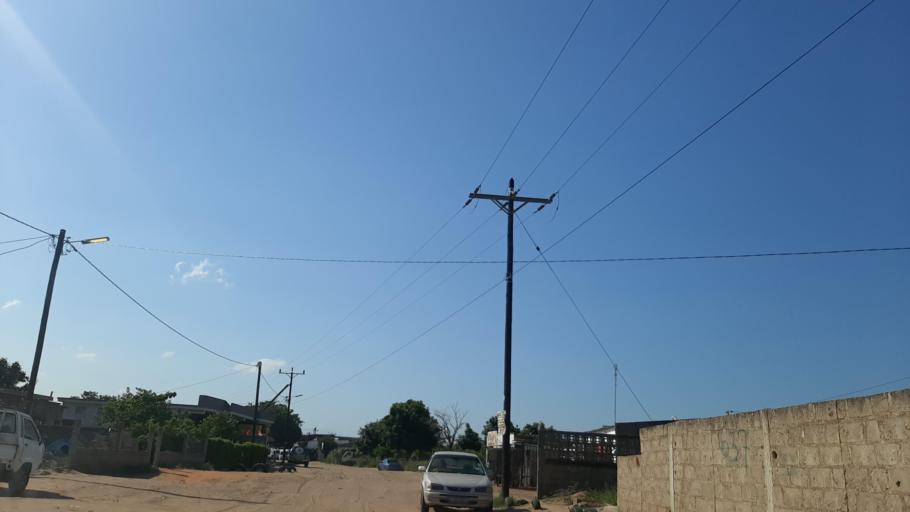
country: MZ
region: Maputo
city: Matola
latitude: -25.7935
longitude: 32.4887
